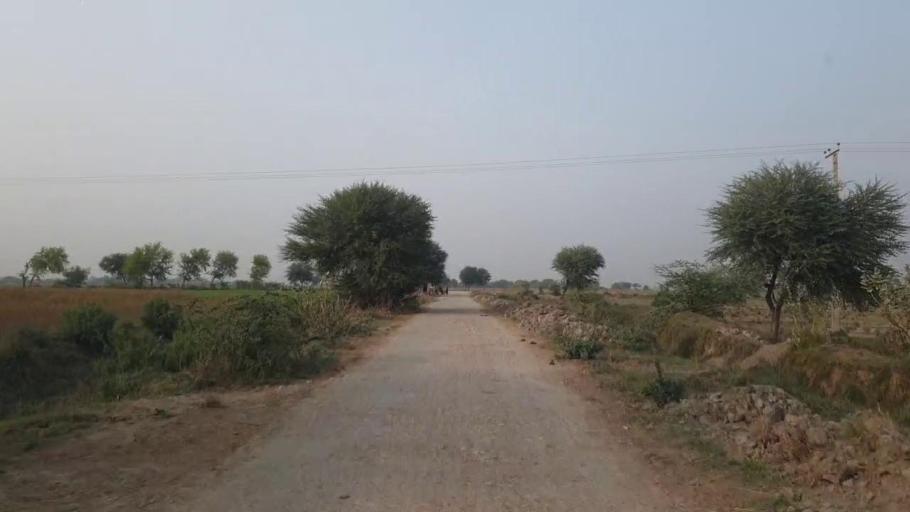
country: PK
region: Sindh
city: Mirpur Batoro
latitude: 24.6591
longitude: 68.3786
